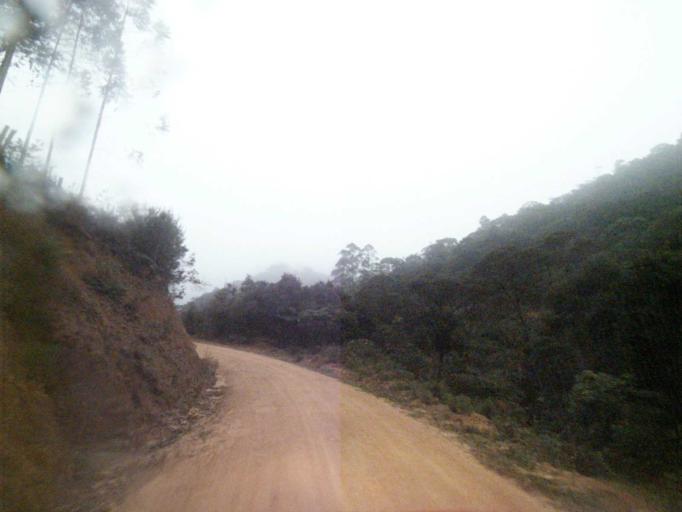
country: BR
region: Santa Catarina
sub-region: Anitapolis
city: Anitapolis
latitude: -27.8211
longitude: -49.1346
